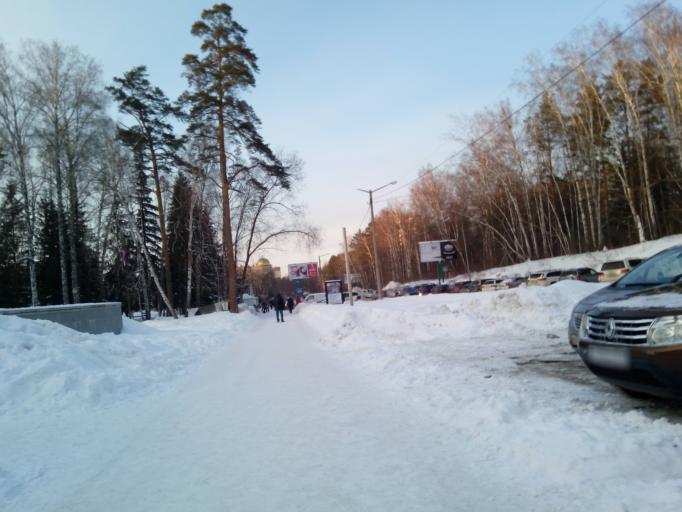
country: RU
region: Novosibirsk
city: Akademgorodok
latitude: 54.8382
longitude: 83.0975
